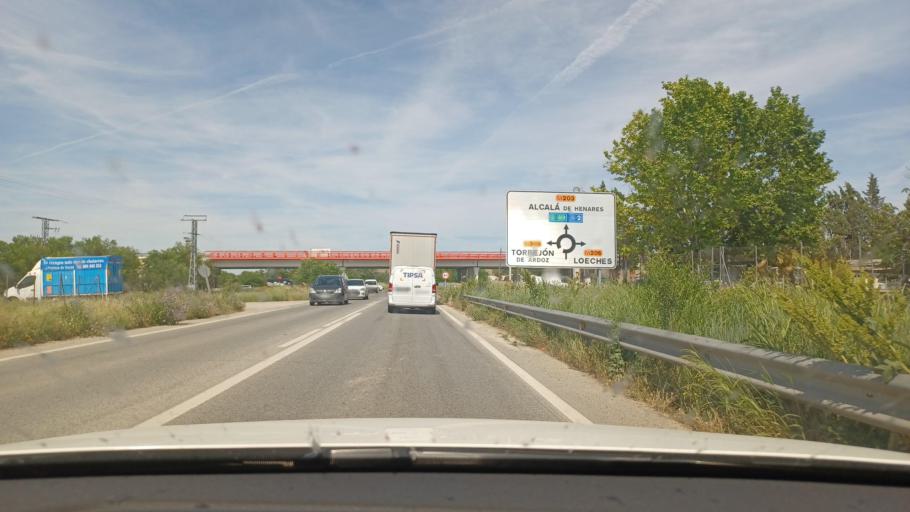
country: ES
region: Madrid
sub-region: Provincia de Madrid
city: Torrejon de Ardoz
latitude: 40.4295
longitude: -3.4466
